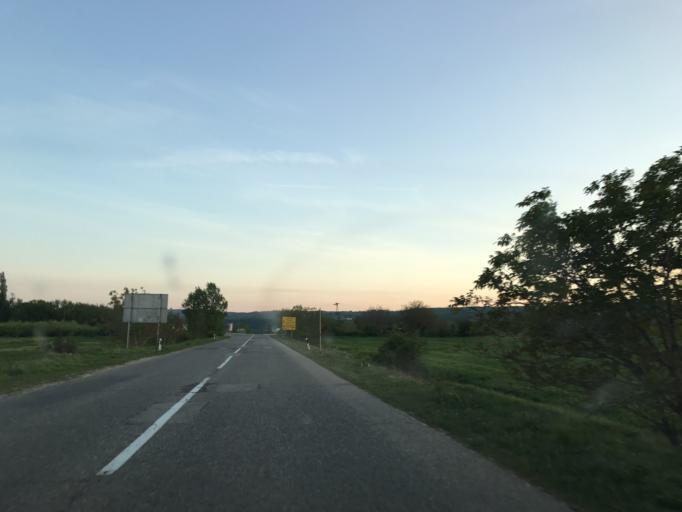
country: RS
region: Central Serbia
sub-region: Borski Okrug
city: Negotin
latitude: 44.2435
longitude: 22.5169
